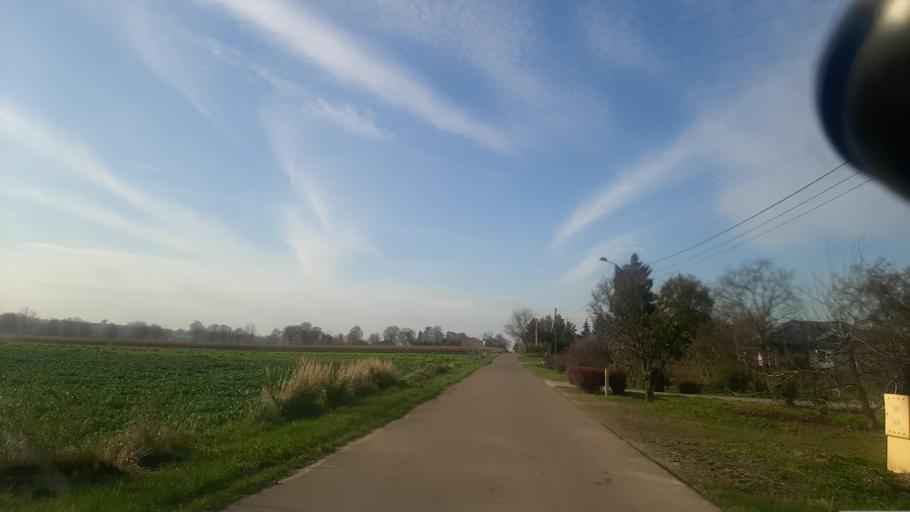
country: PL
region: Lublin Voivodeship
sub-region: Powiat pulawski
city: Markuszow
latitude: 51.3643
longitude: 22.2864
